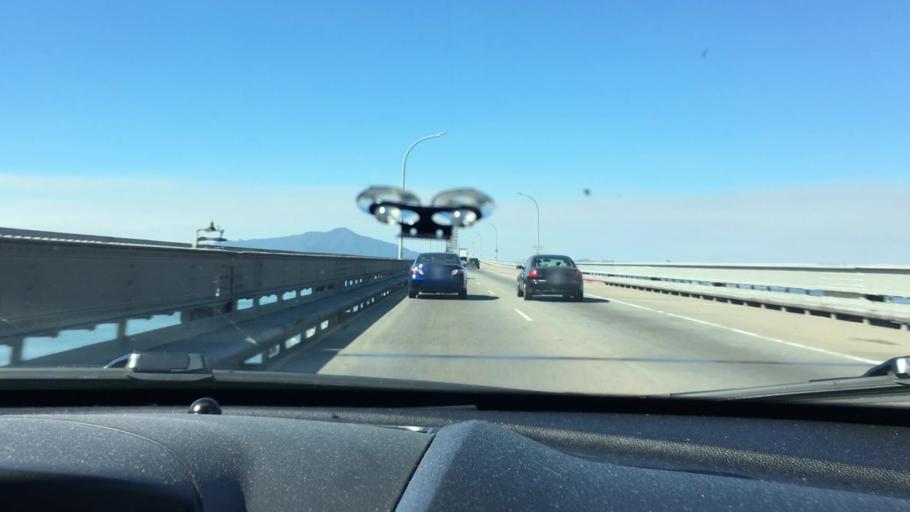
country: US
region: California
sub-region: Contra Costa County
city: North Richmond
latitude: 37.9330
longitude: -122.4132
